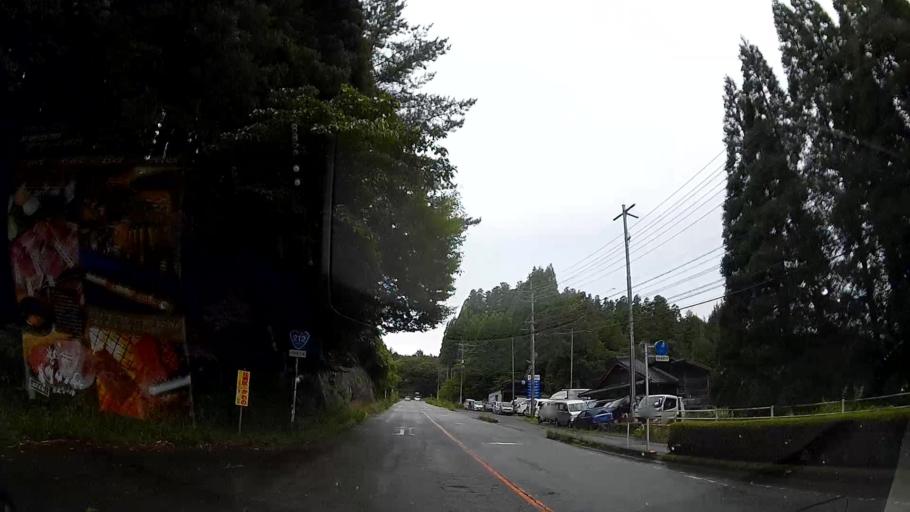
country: JP
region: Oita
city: Tsukawaki
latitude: 33.1394
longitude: 131.0625
